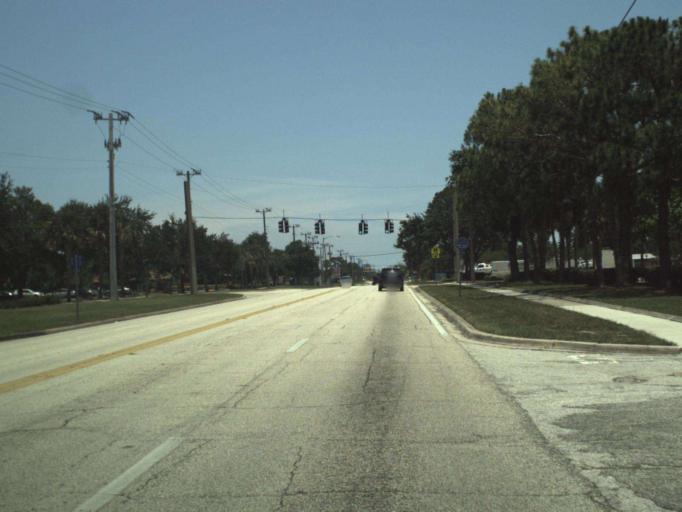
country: US
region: Florida
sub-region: Brevard County
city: West Melbourne
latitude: 28.1216
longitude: -80.6455
